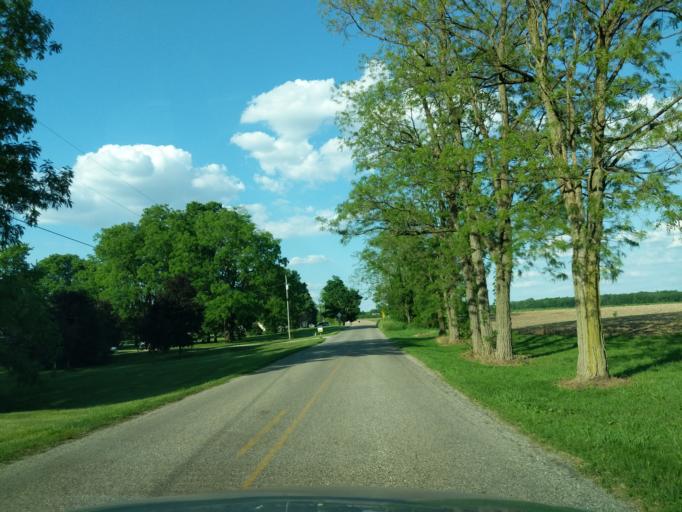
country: US
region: Indiana
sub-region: Kosciusko County
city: North Webster
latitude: 41.3071
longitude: -85.6357
